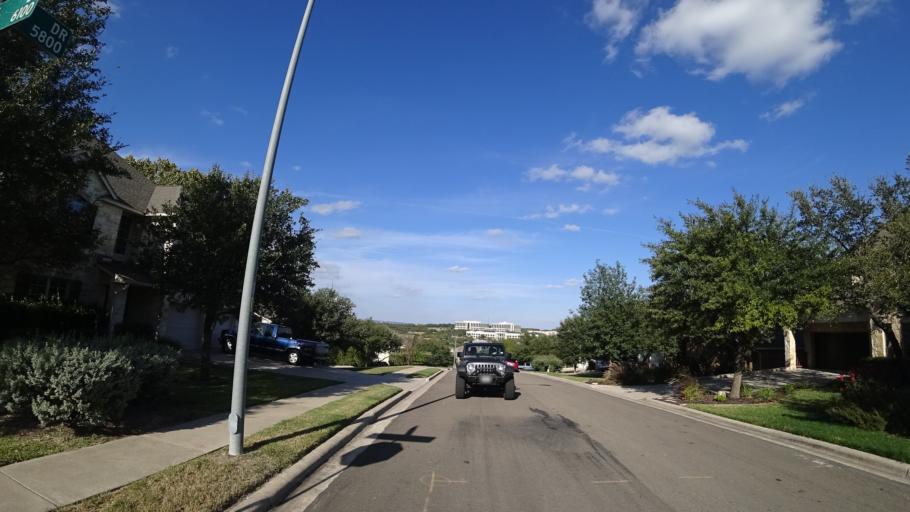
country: US
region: Texas
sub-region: Travis County
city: Barton Creek
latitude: 30.2487
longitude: -97.8758
